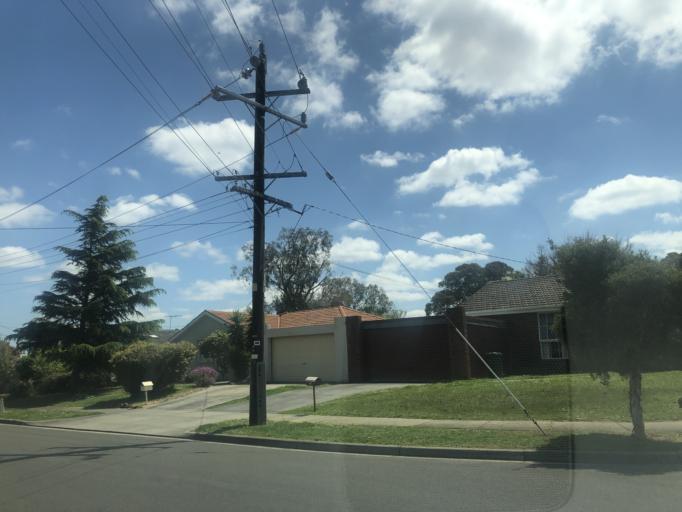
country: AU
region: Victoria
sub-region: Monash
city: Mulgrave
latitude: -37.9136
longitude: 145.1855
